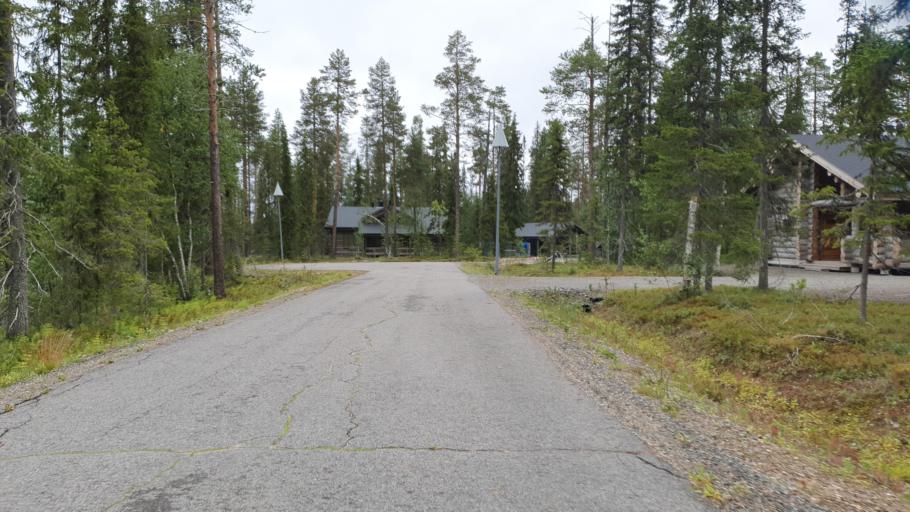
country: FI
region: Lapland
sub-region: Tunturi-Lappi
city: Kolari
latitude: 67.6003
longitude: 24.1818
